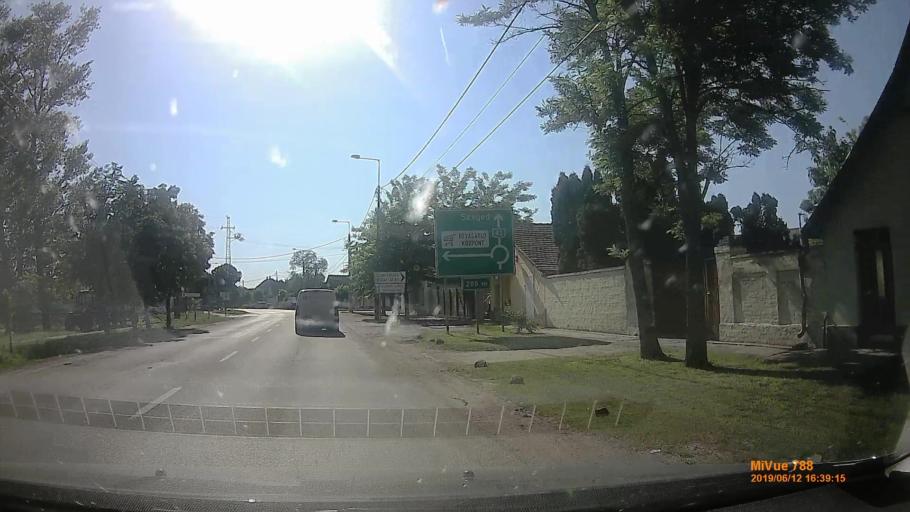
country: HU
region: Csongrad
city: Mako
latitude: 46.2173
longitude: 20.5048
